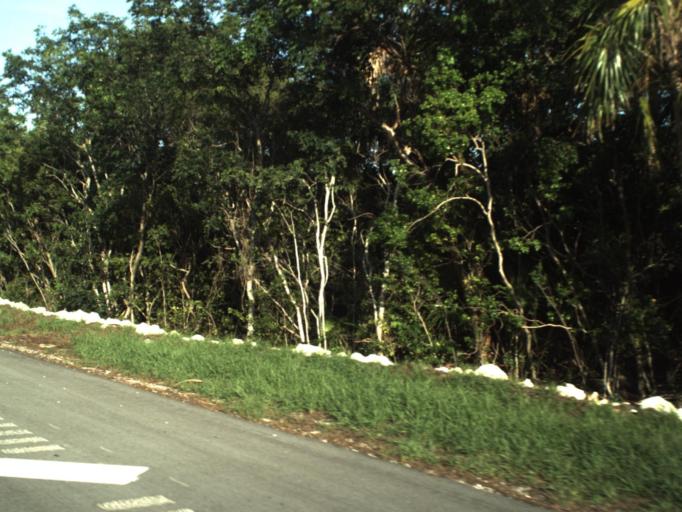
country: US
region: Florida
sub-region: Monroe County
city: Marathon
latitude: 24.7446
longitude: -80.9879
